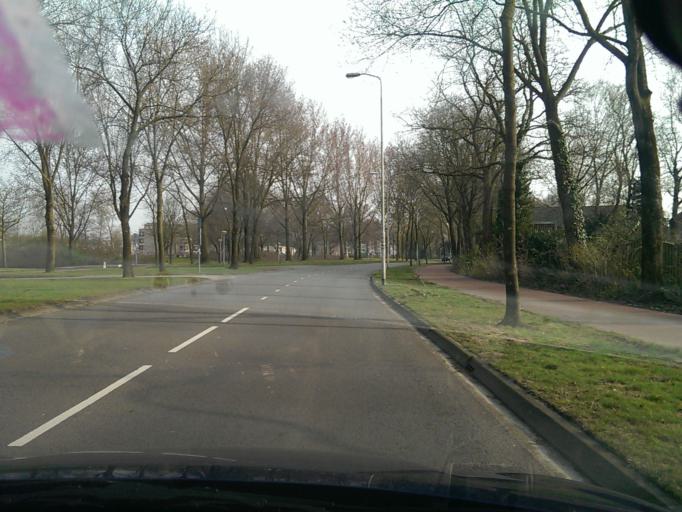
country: NL
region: North Brabant
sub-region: Gemeente Eindhoven
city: Eindhoven
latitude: 51.4246
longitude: 5.4442
